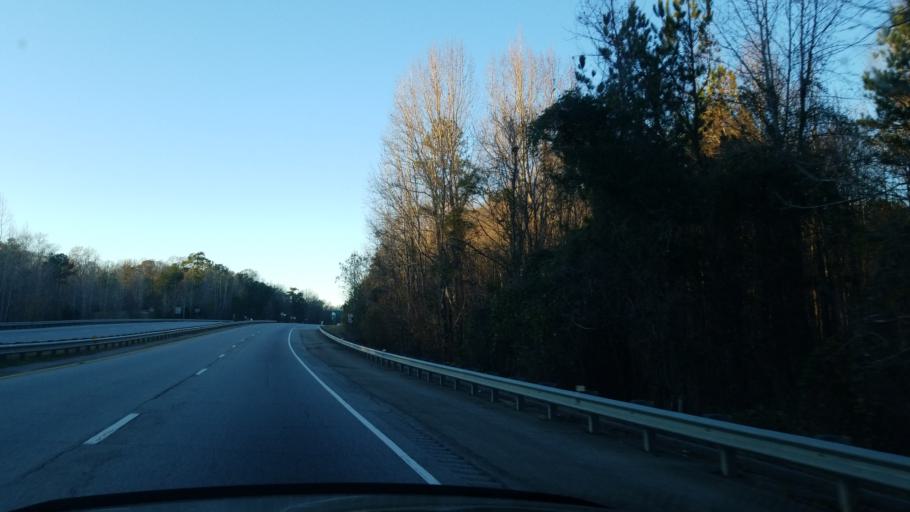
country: US
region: Georgia
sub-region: Chattahoochee County
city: Cusseta
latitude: 32.3121
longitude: -84.7971
